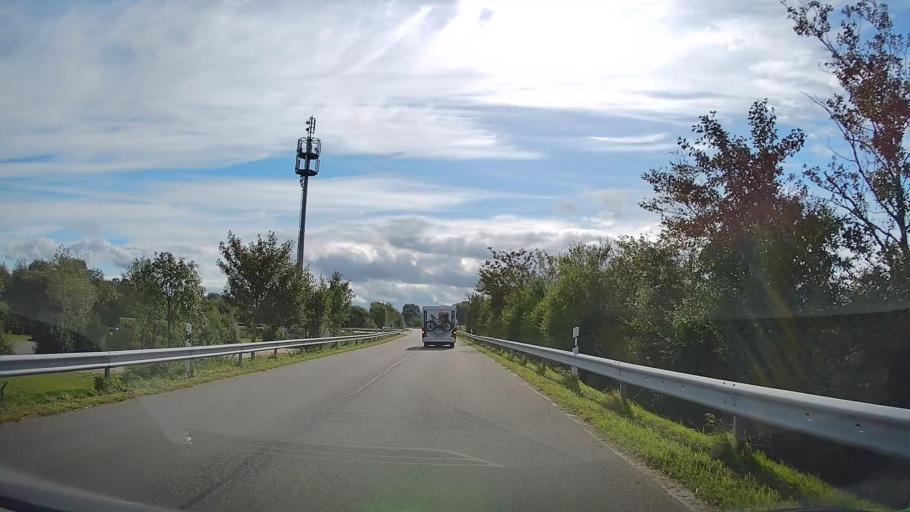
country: DE
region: Schleswig-Holstein
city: Glucksburg
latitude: 54.8581
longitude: 9.5878
